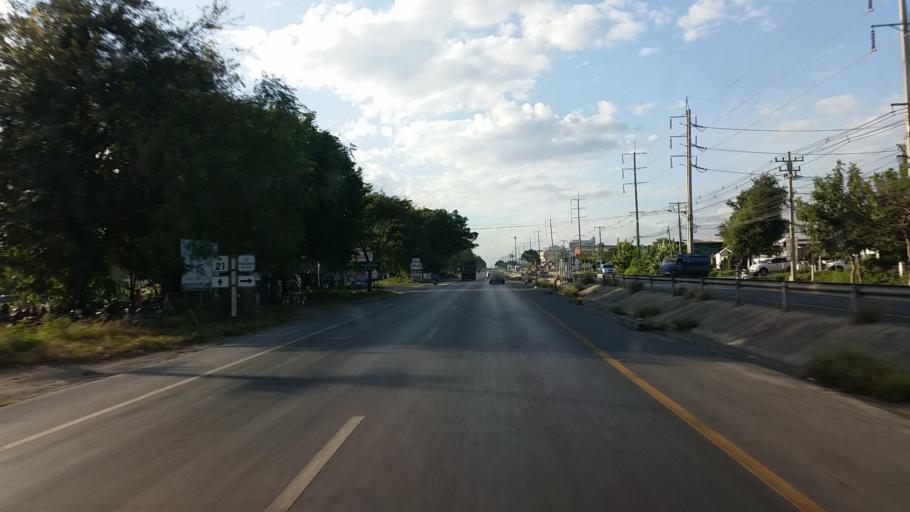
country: TH
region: Lop Buri
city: Phatthana Nikhom
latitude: 14.8289
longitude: 100.9107
